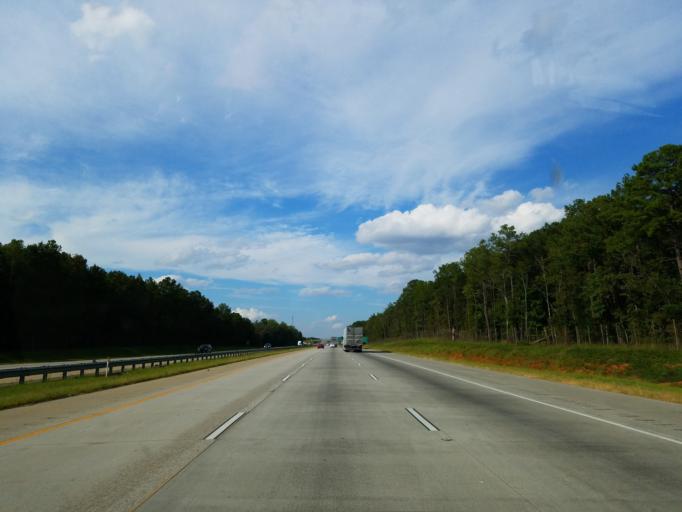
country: US
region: Georgia
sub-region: Dooly County
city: Unadilla
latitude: 32.3271
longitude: -83.7659
